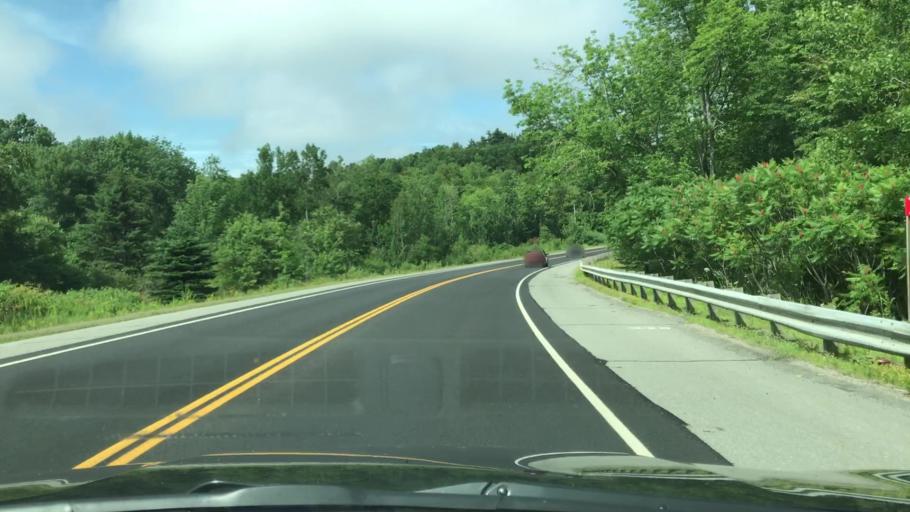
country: US
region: Maine
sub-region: Hancock County
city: Bucksport
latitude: 44.5546
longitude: -68.8100
